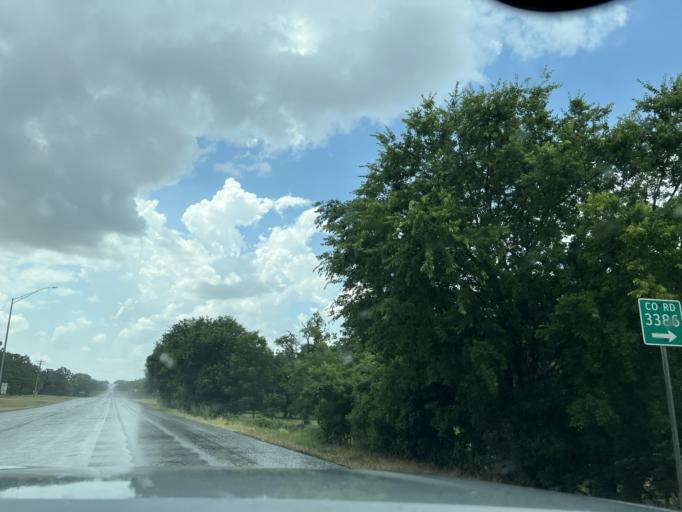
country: US
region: Texas
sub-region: Wise County
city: Boyd
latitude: 33.1094
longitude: -97.6581
